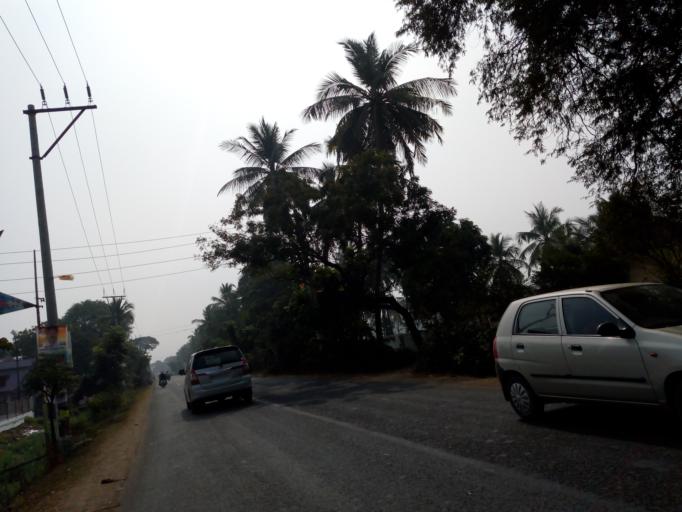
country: IN
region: Andhra Pradesh
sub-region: West Godavari
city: Bhimavaram
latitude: 16.5843
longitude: 81.4708
